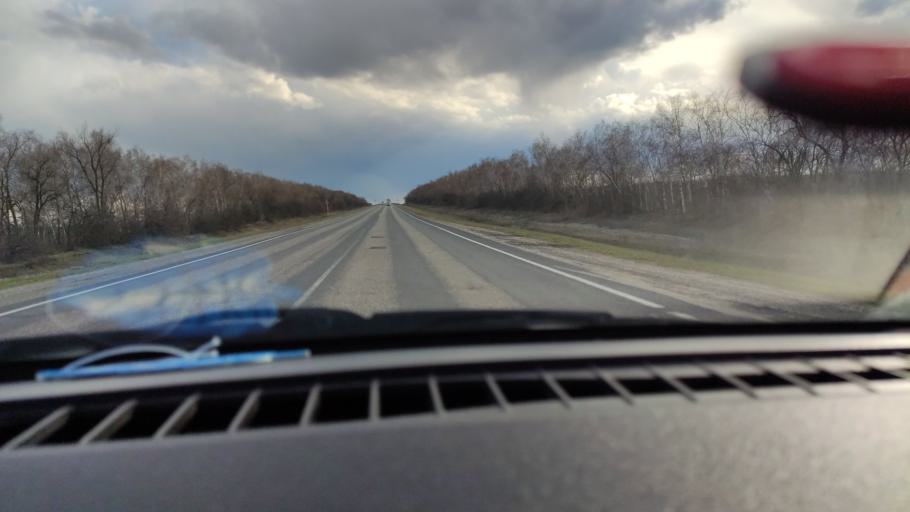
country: RU
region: Saratov
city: Sinodskoye
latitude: 51.9454
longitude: 46.6018
